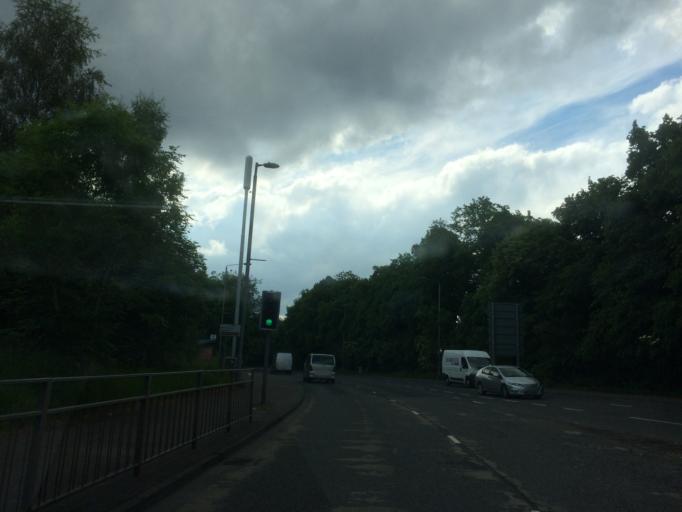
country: GB
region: Scotland
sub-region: East Renfrewshire
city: Giffnock
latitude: 55.8386
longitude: -4.3076
